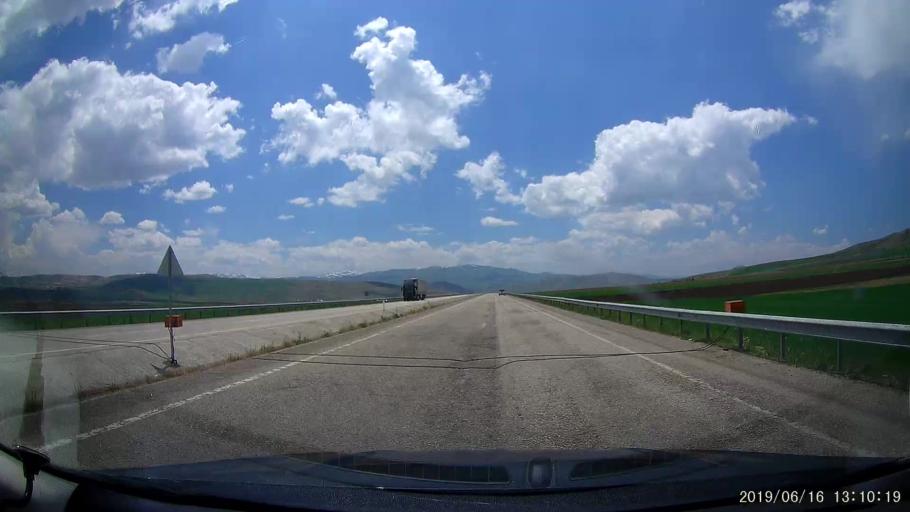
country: TR
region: Agri
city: Diyadin
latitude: 39.5961
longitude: 43.6354
